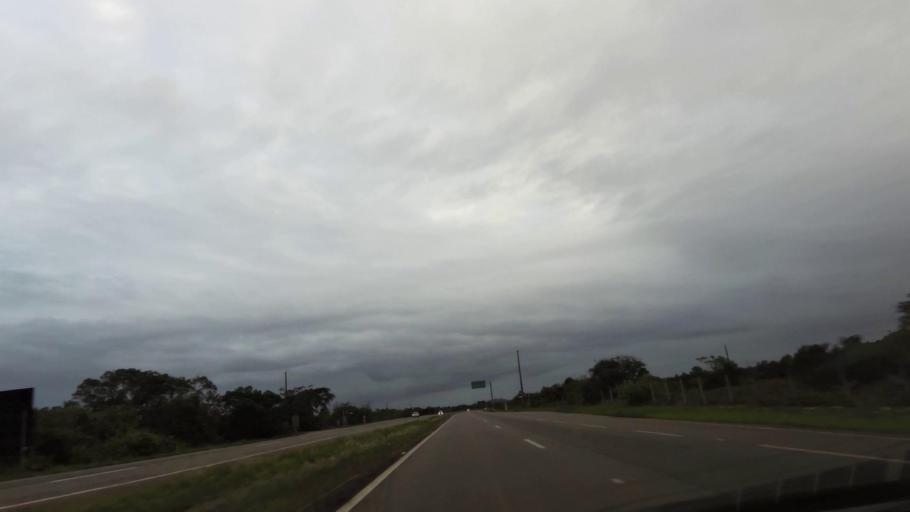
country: BR
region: Espirito Santo
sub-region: Guarapari
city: Guarapari
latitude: -20.6019
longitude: -40.4264
